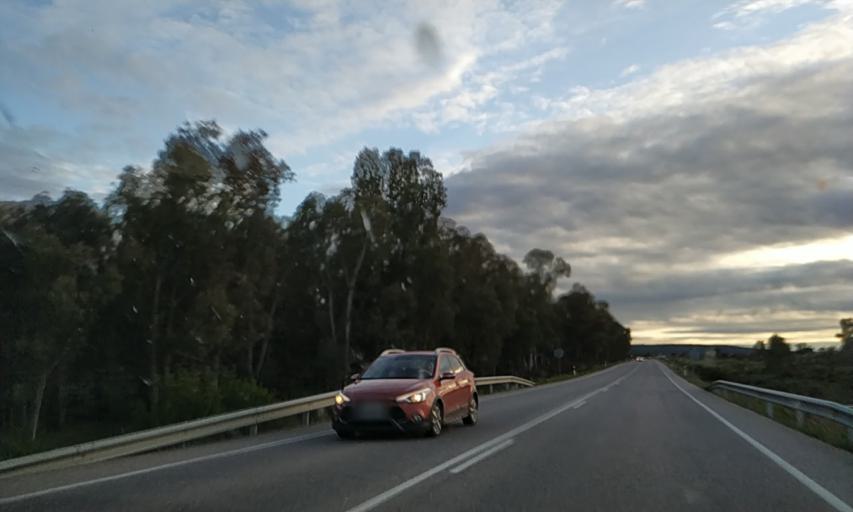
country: ES
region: Extremadura
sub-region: Provincia de Caceres
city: Malpartida de Caceres
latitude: 39.3290
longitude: -6.4899
